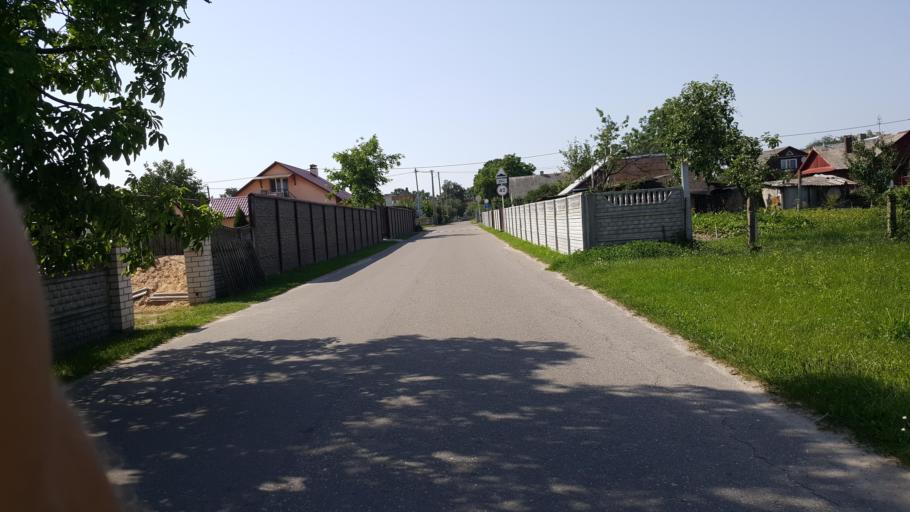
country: BY
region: Brest
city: Zhabinka
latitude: 52.2006
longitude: 24.0234
